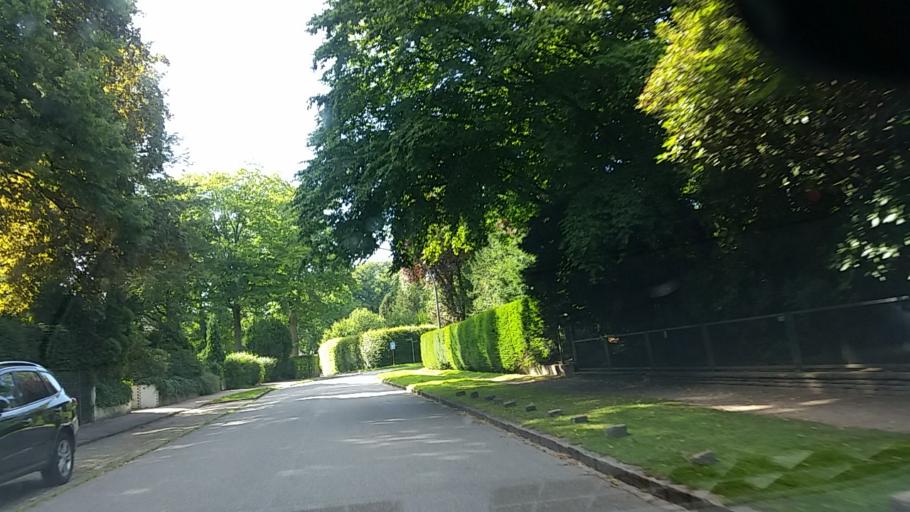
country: DE
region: Schleswig-Holstein
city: Halstenbek
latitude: 53.5629
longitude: 9.8410
